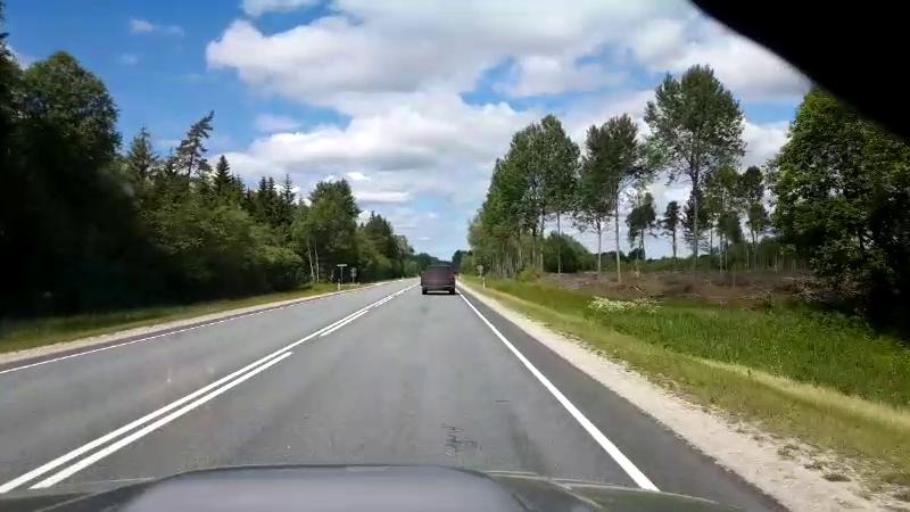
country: EE
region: Raplamaa
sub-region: Maerjamaa vald
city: Marjamaa
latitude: 59.0351
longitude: 24.4440
